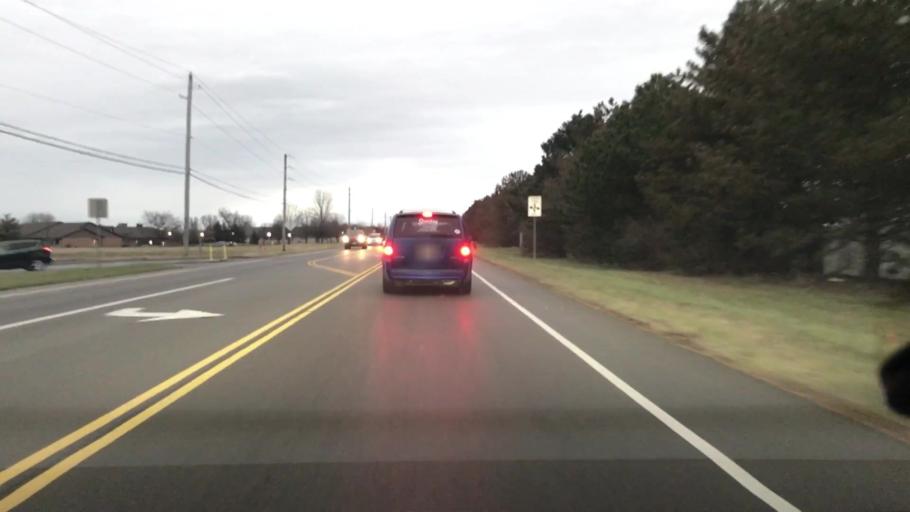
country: US
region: Ohio
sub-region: Clark County
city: Holiday Valley
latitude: 39.8617
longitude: -83.9646
